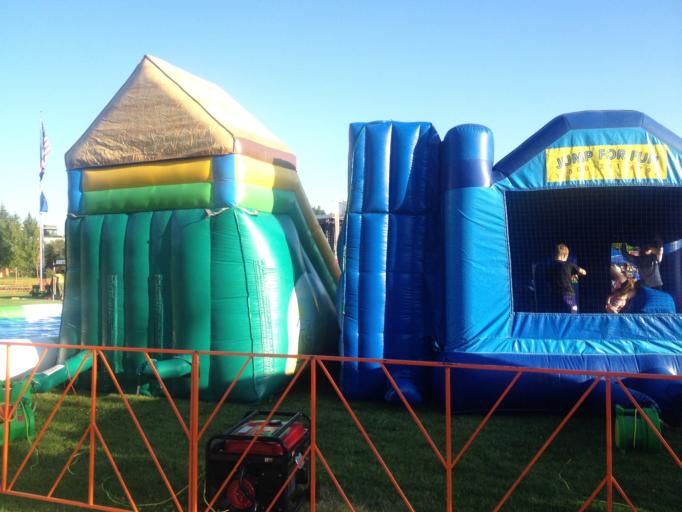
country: US
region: Colorado
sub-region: Boulder County
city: Longmont
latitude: 40.1723
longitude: -105.1058
